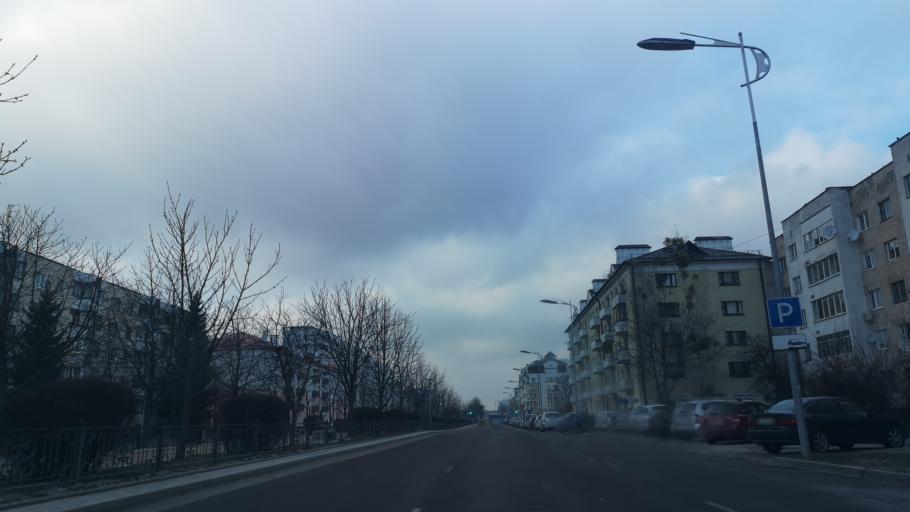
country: BY
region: Brest
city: Brest
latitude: 52.0949
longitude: 23.6991
